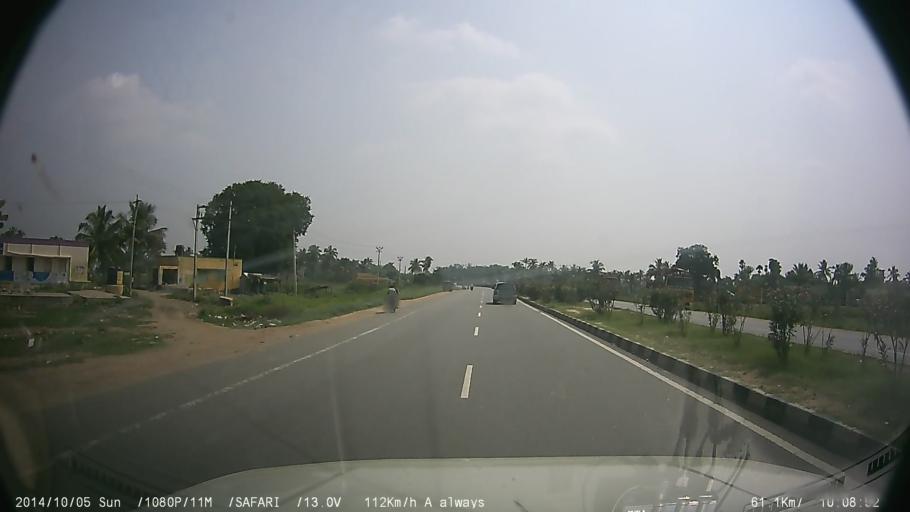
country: IN
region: Tamil Nadu
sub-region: Salem
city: Konganapuram
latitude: 11.5209
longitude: 77.9377
